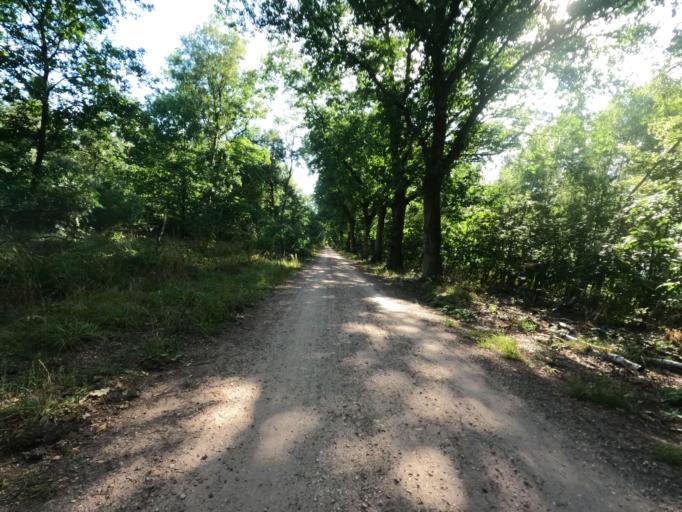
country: NL
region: Limburg
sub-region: Gemeente Beesel
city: Offenbeek
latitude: 51.2557
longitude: 6.0971
